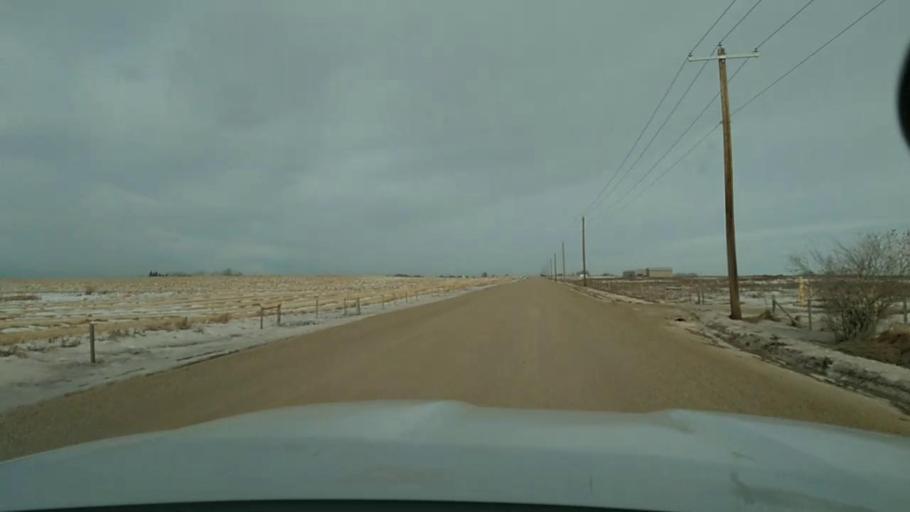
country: CA
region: Alberta
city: Airdrie
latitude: 51.2195
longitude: -113.9118
